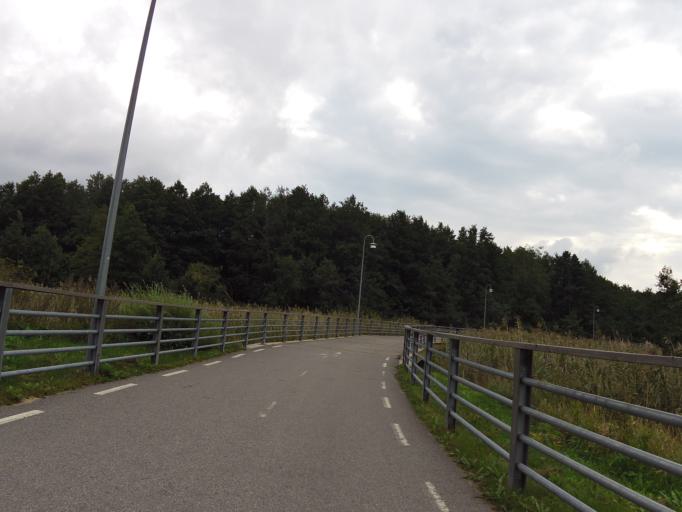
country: EE
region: Harju
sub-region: Tallinna linn
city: Tallinn
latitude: 59.4321
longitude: 24.6775
